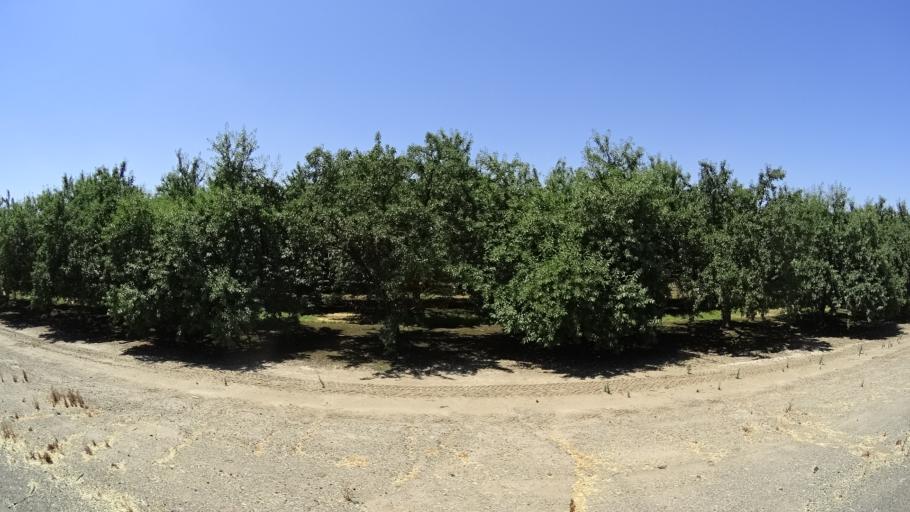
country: US
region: California
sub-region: Kings County
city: Lucerne
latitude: 36.4034
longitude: -119.6010
